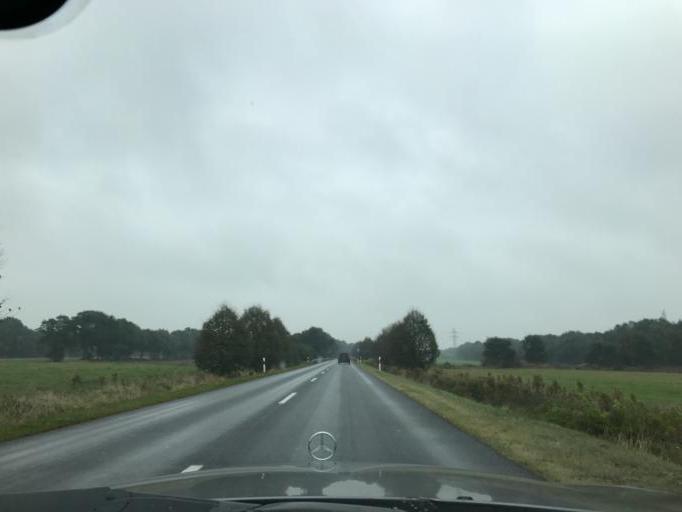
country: DE
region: Lower Saxony
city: Weener
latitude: 53.1307
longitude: 7.3073
